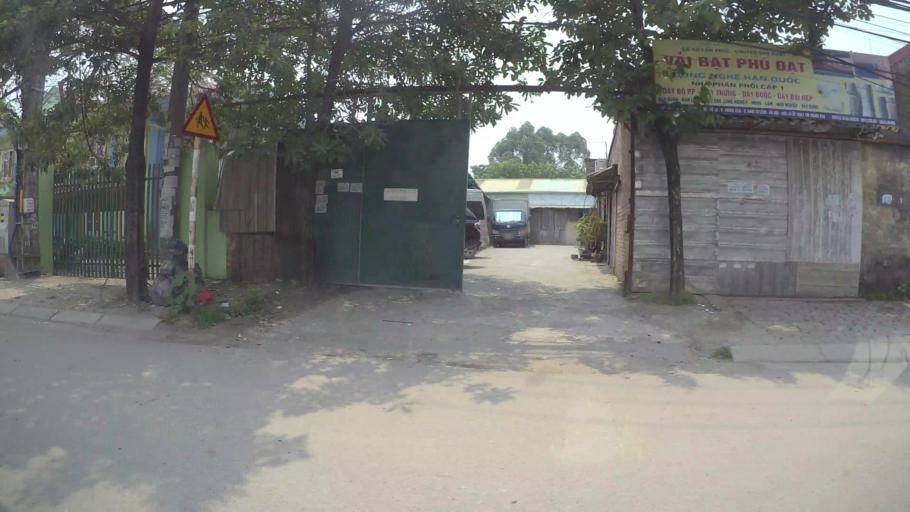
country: VN
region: Ha Noi
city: Ha Dong
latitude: 20.9940
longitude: 105.7738
